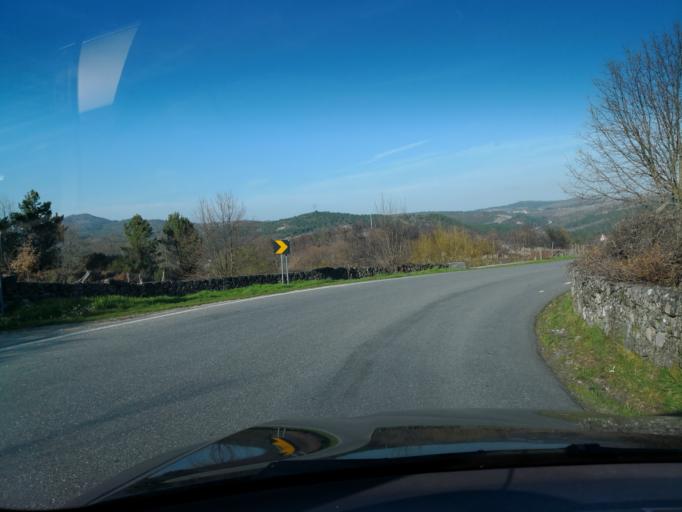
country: PT
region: Vila Real
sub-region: Sabrosa
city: Sabrosa
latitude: 41.3527
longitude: -7.6027
